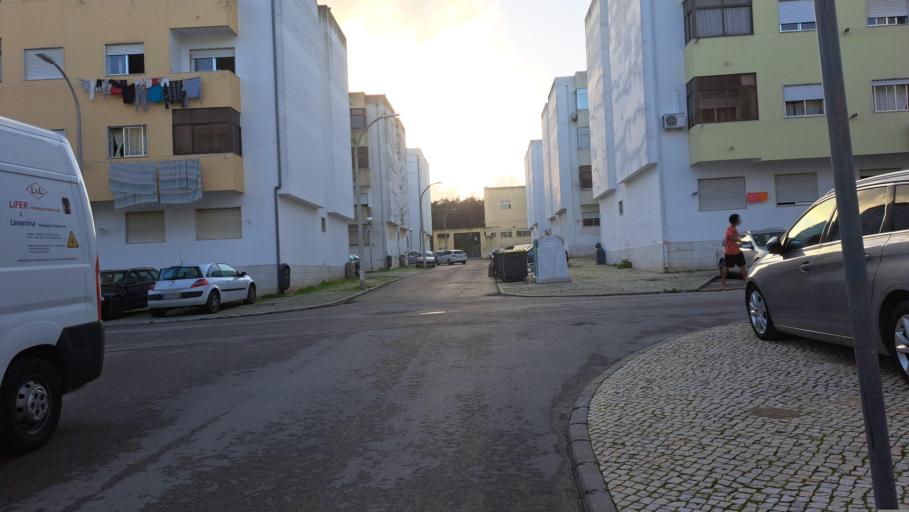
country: PT
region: Setubal
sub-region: Moita
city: Alhos Vedros
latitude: 38.6530
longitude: -9.0420
